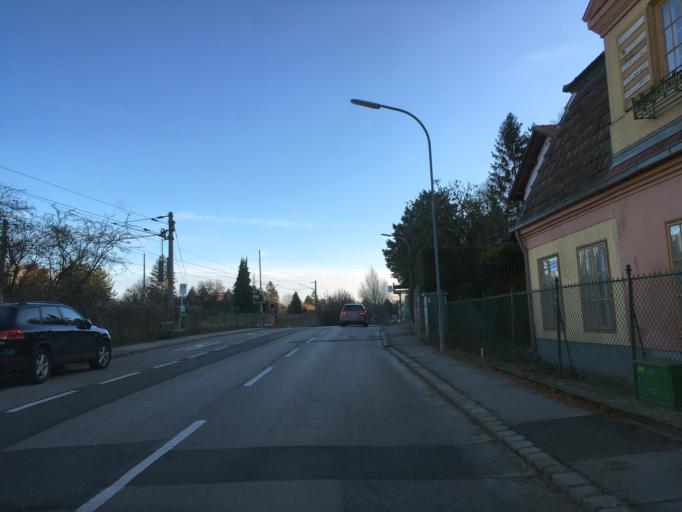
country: AT
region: Lower Austria
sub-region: Politischer Bezirk Korneuburg
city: Korneuburg
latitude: 48.3458
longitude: 16.2892
